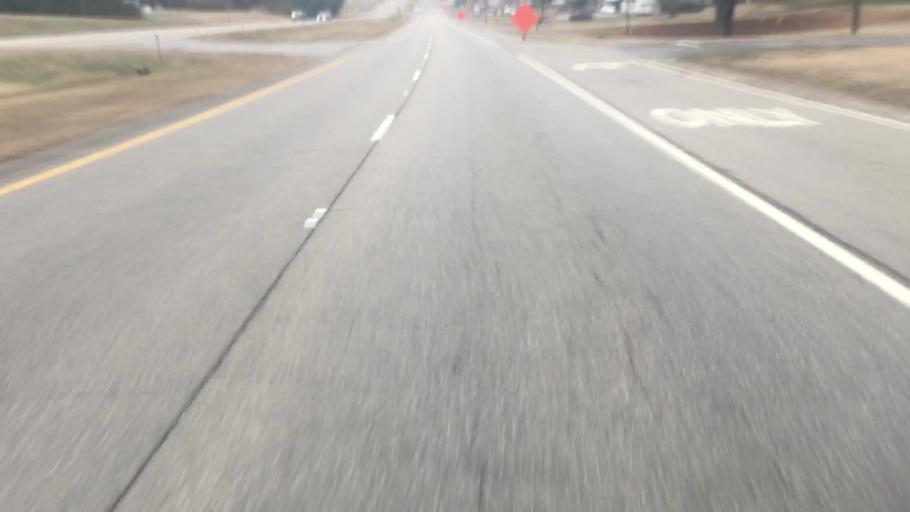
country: US
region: Alabama
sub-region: Walker County
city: Sumiton
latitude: 33.7615
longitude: -87.0677
